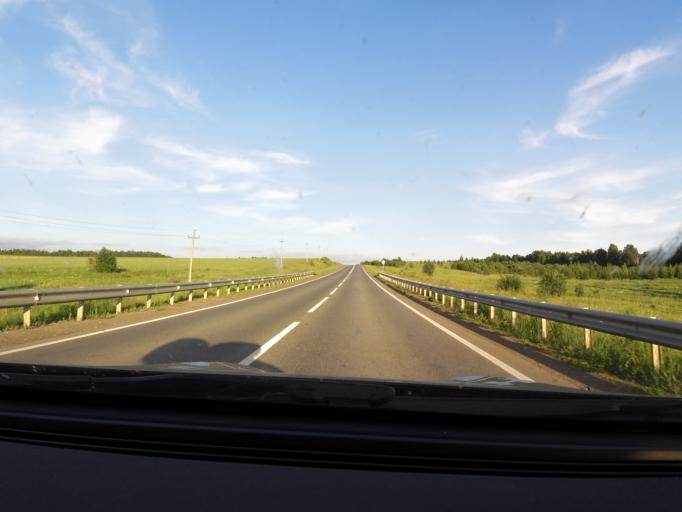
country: RU
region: Perm
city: Siva
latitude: 58.5323
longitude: 53.9749
